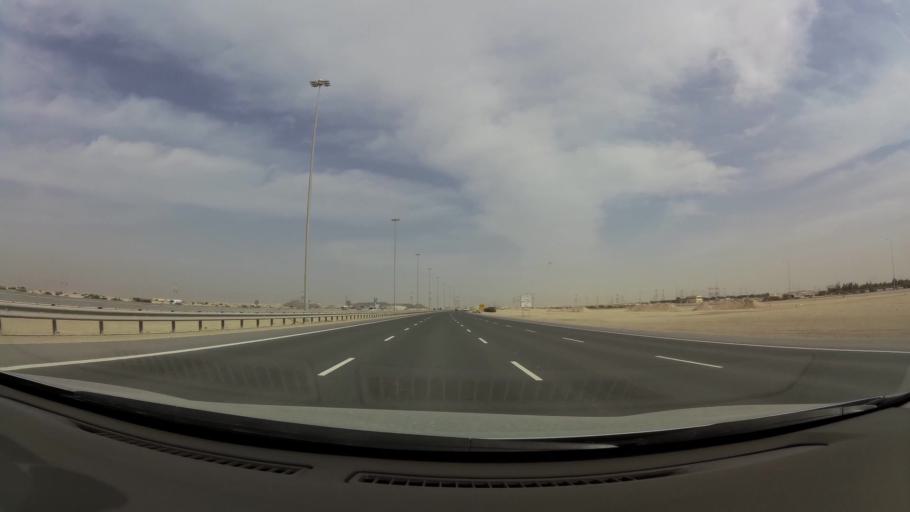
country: QA
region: Baladiyat ar Rayyan
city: Ash Shahaniyah
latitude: 25.3499
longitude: 51.2988
